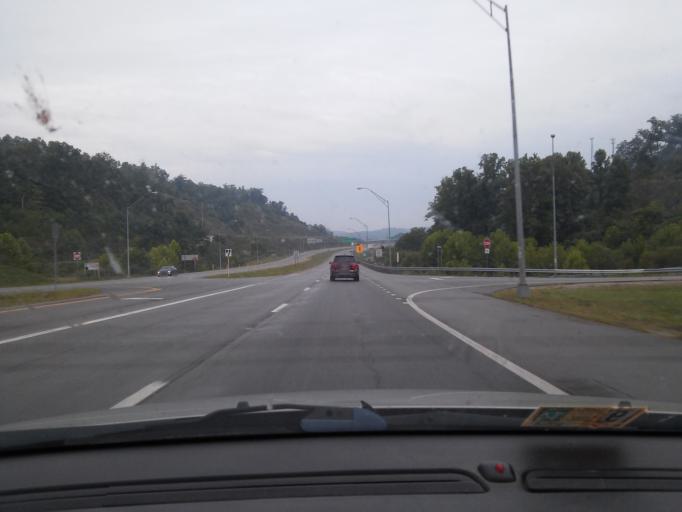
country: US
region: West Virginia
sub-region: Putnam County
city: Teays Valley
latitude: 38.4635
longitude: -81.9074
